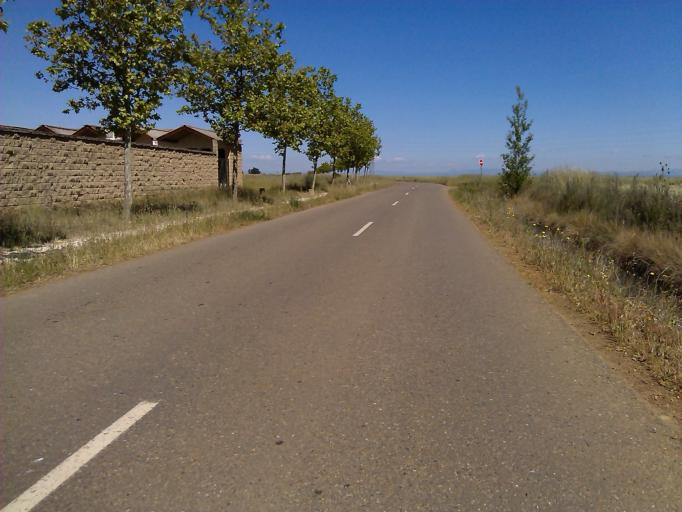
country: ES
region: Castille and Leon
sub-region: Provincia de Leon
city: Vallecillo
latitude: 42.4260
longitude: -5.2270
